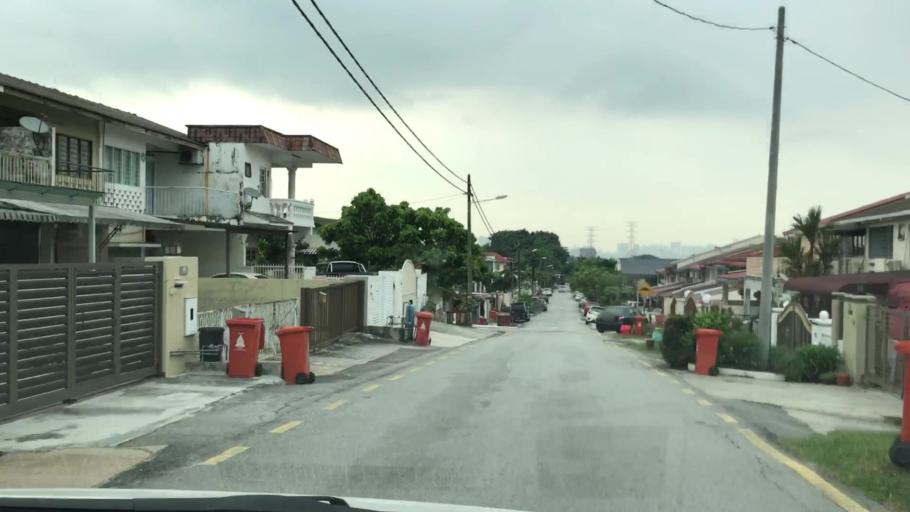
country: MY
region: Selangor
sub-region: Petaling
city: Petaling Jaya
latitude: 3.1101
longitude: 101.6190
